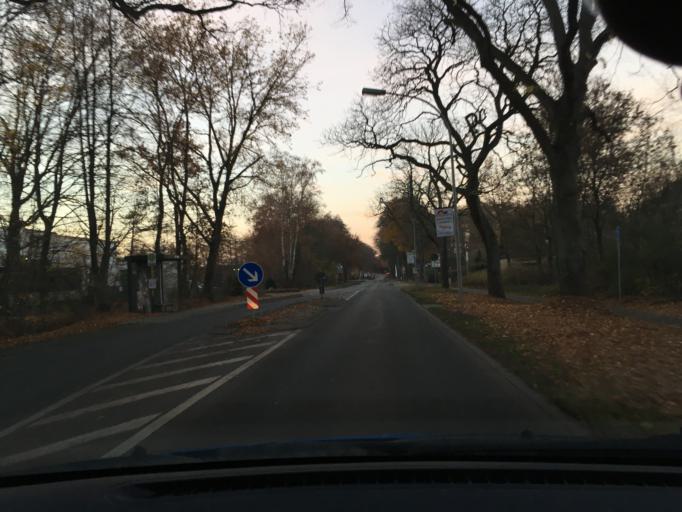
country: DE
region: Lower Saxony
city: Uelzen
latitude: 52.9841
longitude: 10.5499
